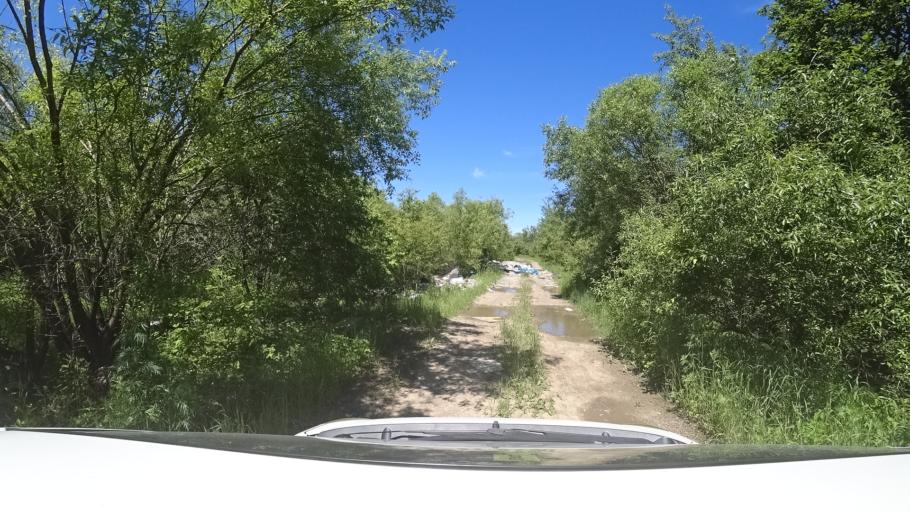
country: RU
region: Khabarovsk Krai
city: Topolevo
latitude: 48.4873
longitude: 135.1770
